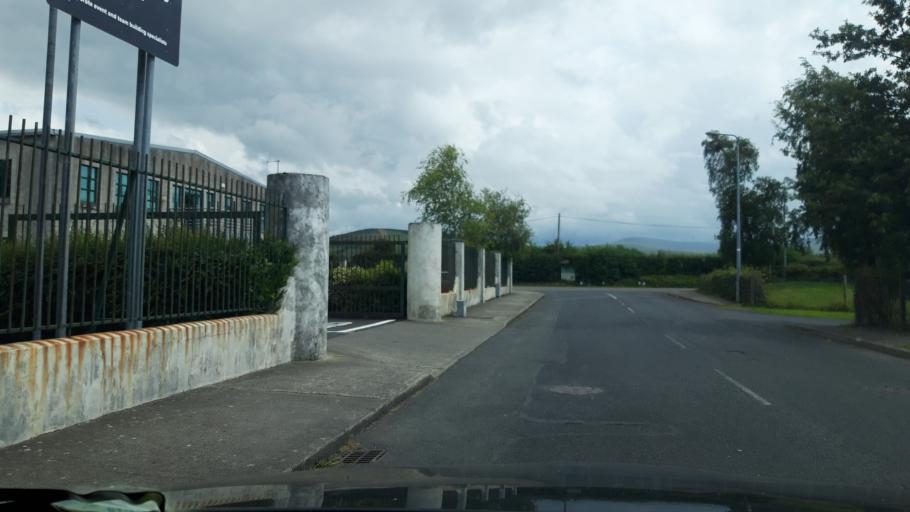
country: IE
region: Leinster
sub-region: Wicklow
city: Blessington
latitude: 53.1638
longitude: -6.5398
